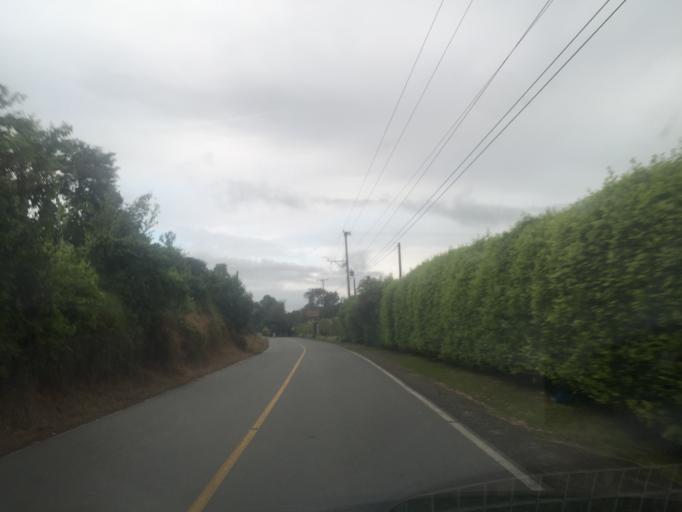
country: CO
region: Quindio
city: Montenegro
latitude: 4.5151
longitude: -75.7384
